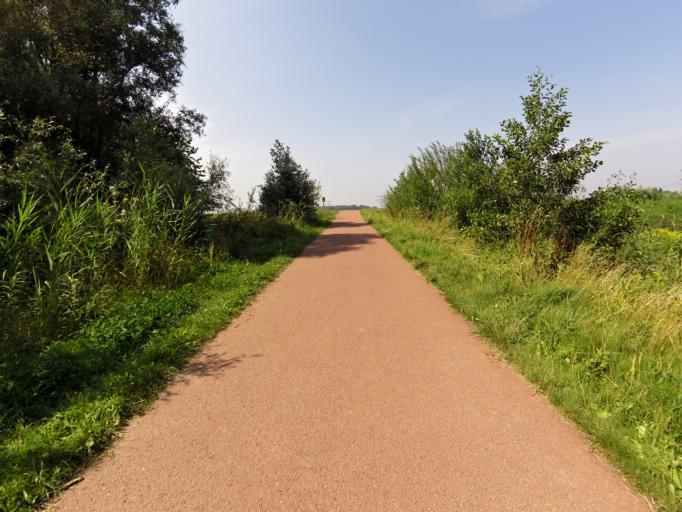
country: NL
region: South Holland
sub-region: Gemeente Dordrecht
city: Dordrecht
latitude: 51.7630
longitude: 4.6848
